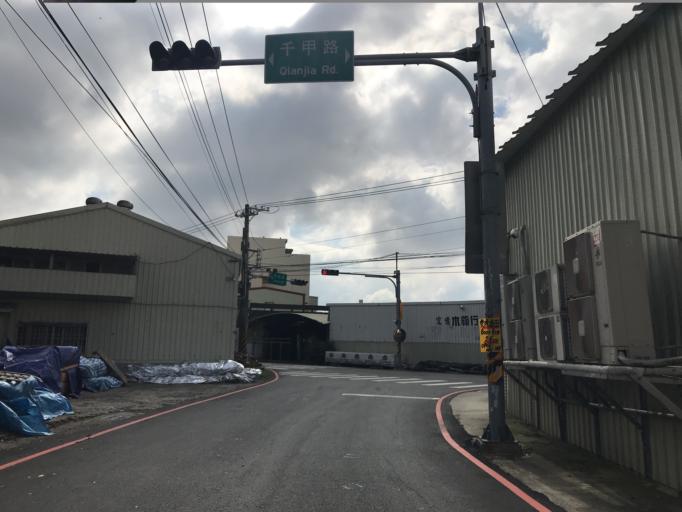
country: TW
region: Taiwan
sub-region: Hsinchu
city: Zhubei
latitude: 24.8080
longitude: 121.0060
